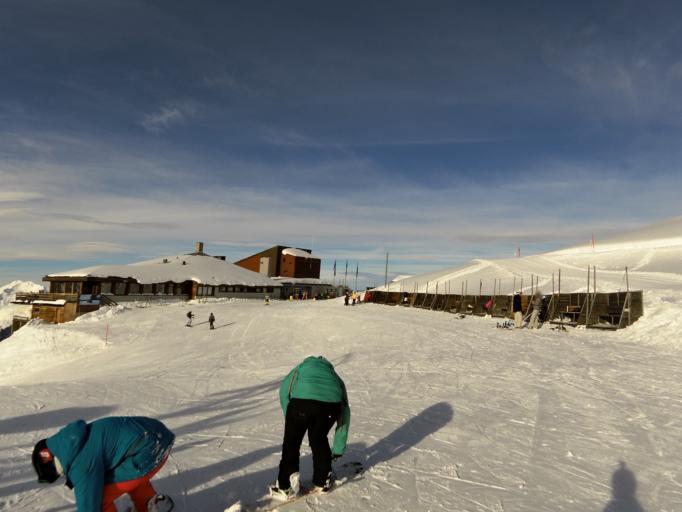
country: CH
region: Grisons
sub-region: Praettigau/Davos District
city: Davos
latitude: 46.8089
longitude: 9.9204
